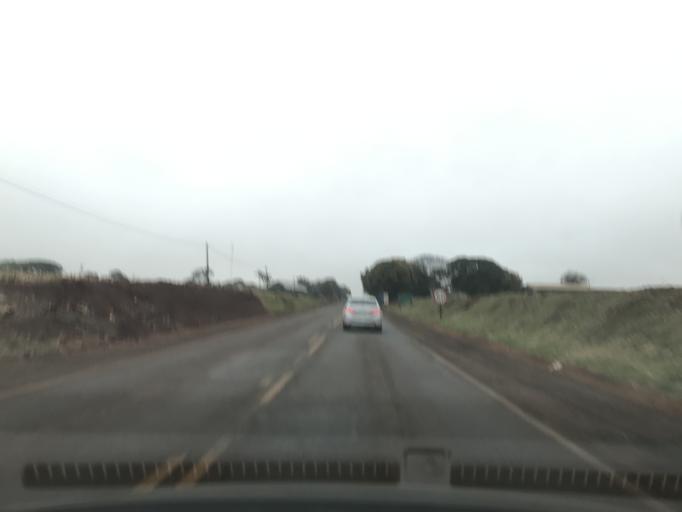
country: BR
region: Parana
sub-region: Palotina
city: Palotina
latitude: -24.3441
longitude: -53.8332
